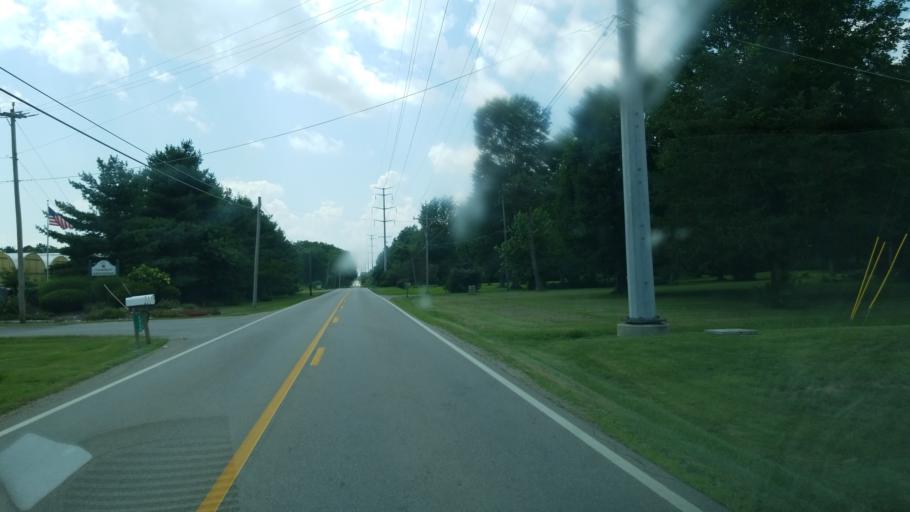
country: US
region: Ohio
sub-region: Delaware County
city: Powell
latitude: 40.2156
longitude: -83.0743
